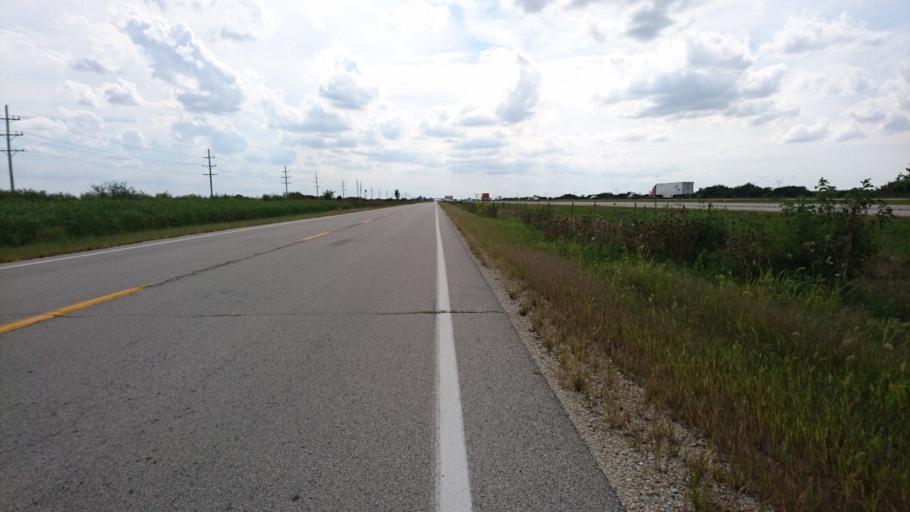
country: US
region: Illinois
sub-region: Grundy County
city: Gardner
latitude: 41.1696
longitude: -88.3316
